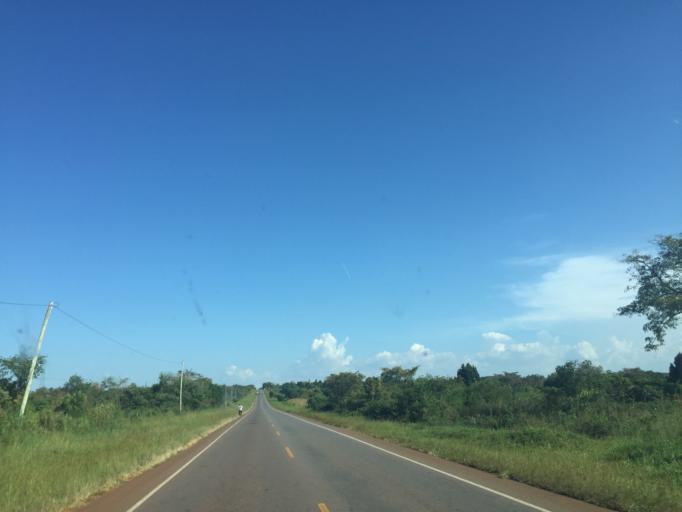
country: UG
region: Central Region
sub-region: Nakasongola District
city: Nakasongola
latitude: 1.3483
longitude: 32.3861
